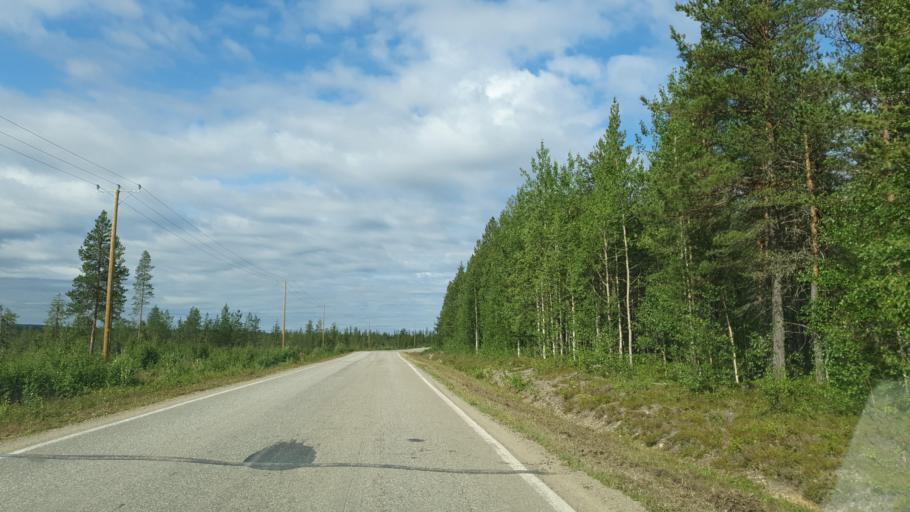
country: FI
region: Lapland
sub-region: Pohjois-Lappi
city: Sodankylae
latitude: 67.5259
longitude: 25.9991
